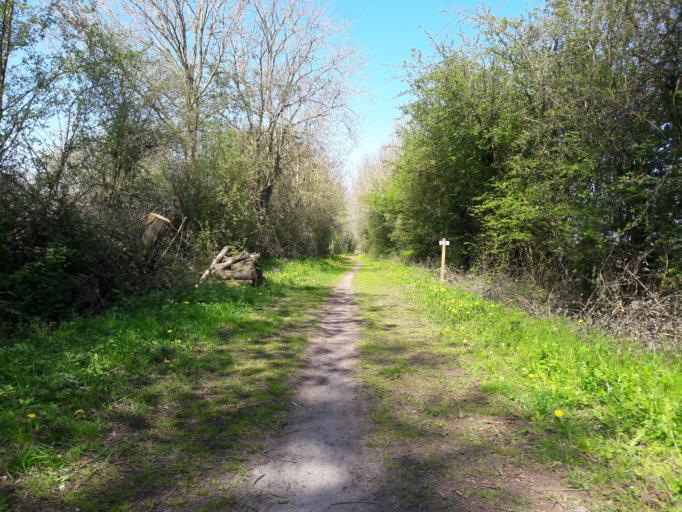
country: FR
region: Nord-Pas-de-Calais
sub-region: Departement du Nord
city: Sains-du-Nord
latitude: 50.1637
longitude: 4.0722
